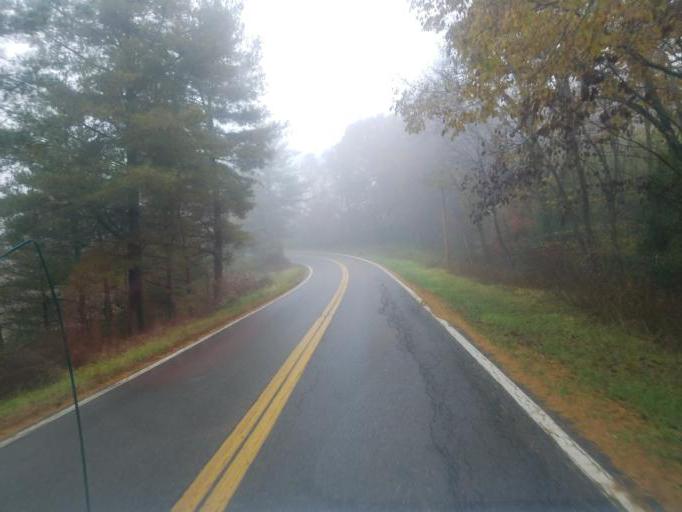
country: US
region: Ohio
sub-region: Morgan County
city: McConnelsville
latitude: 39.5383
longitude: -81.8012
